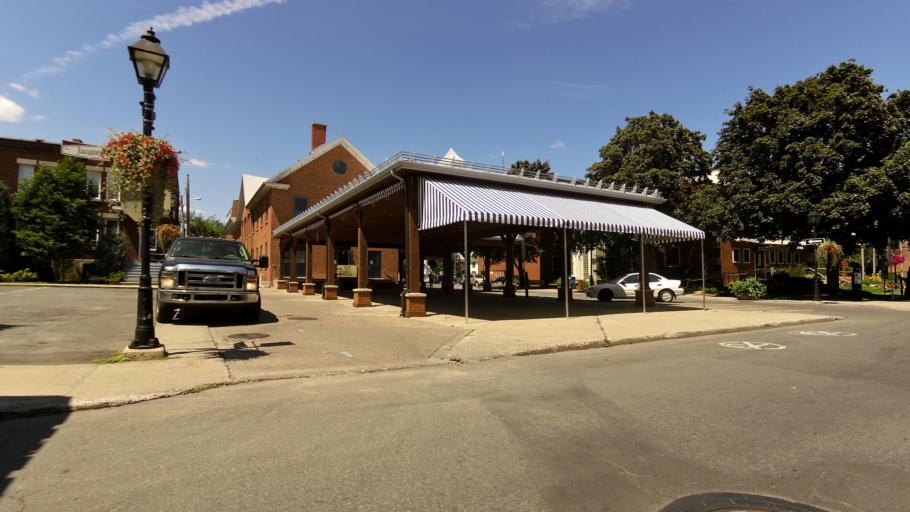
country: CA
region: Quebec
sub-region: Monteregie
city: Saint-Jean-sur-Richelieu
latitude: 45.3052
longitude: -73.2534
